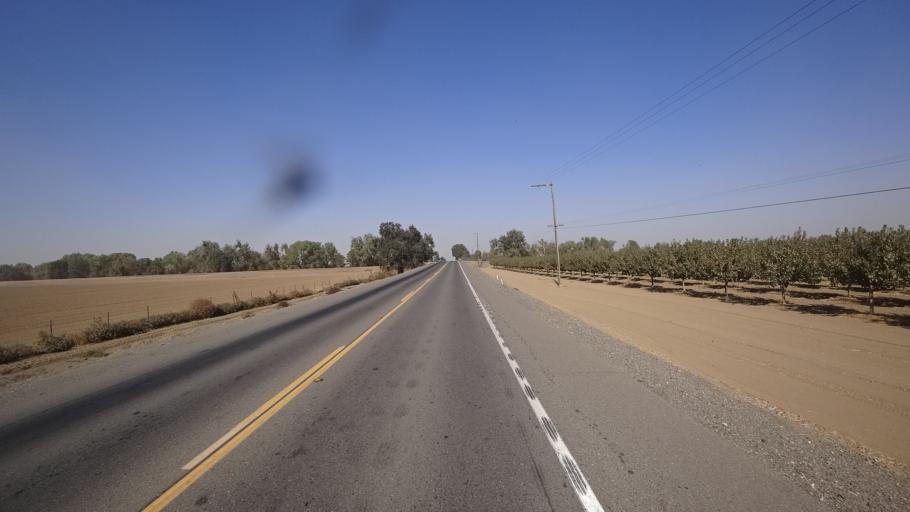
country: US
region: California
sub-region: Yolo County
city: Woodland
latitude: 38.7243
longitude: -121.7300
